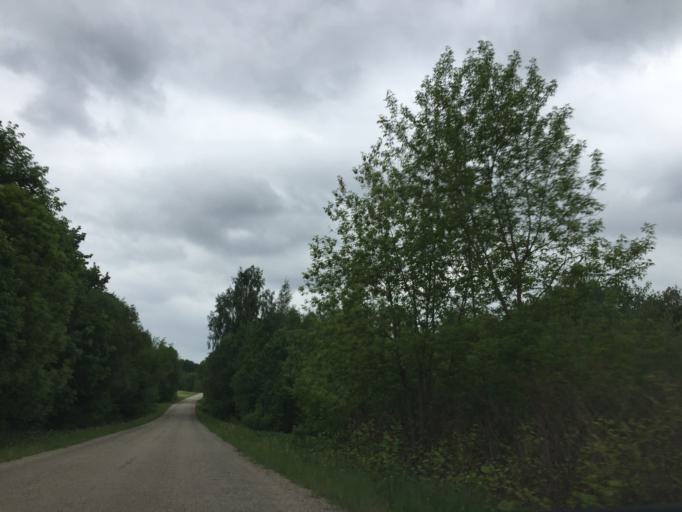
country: LV
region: Aglona
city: Aglona
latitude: 56.0823
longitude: 26.9186
